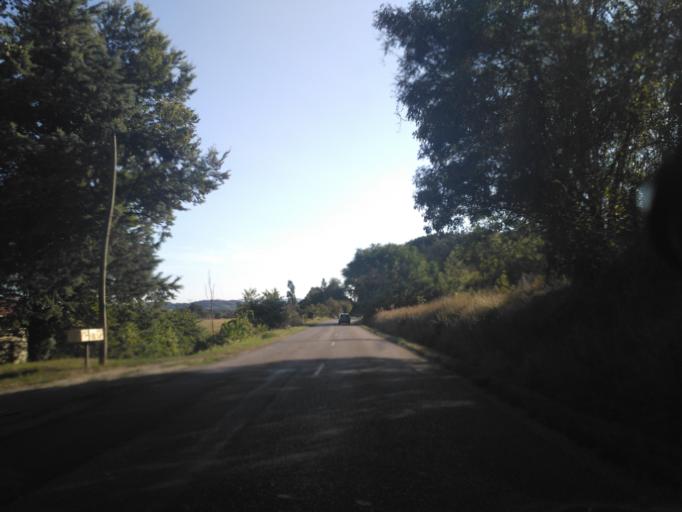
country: FR
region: Rhone-Alpes
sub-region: Departement de la Drome
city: Clerieux
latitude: 45.1125
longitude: 4.9592
